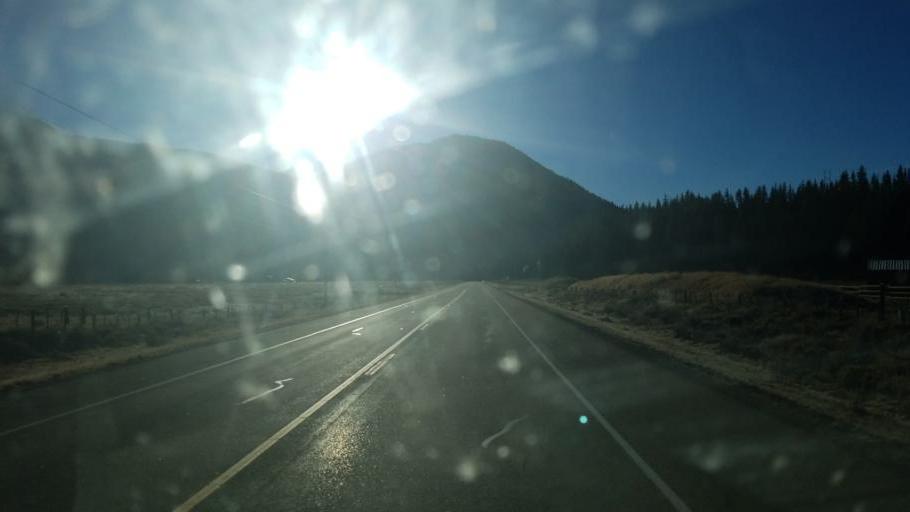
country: US
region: Colorado
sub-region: Gunnison County
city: Crested Butte
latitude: 38.8016
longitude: -106.8863
